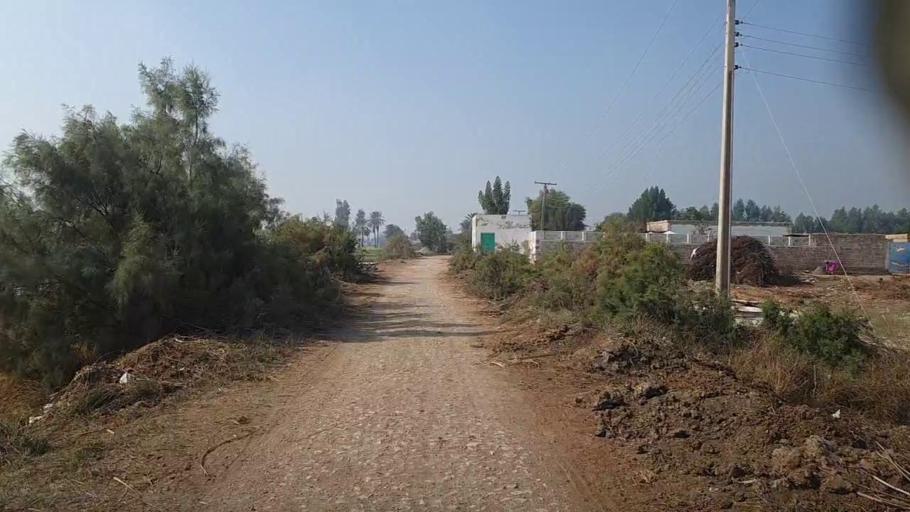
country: PK
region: Sindh
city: Khairpur
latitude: 27.9263
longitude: 69.6652
